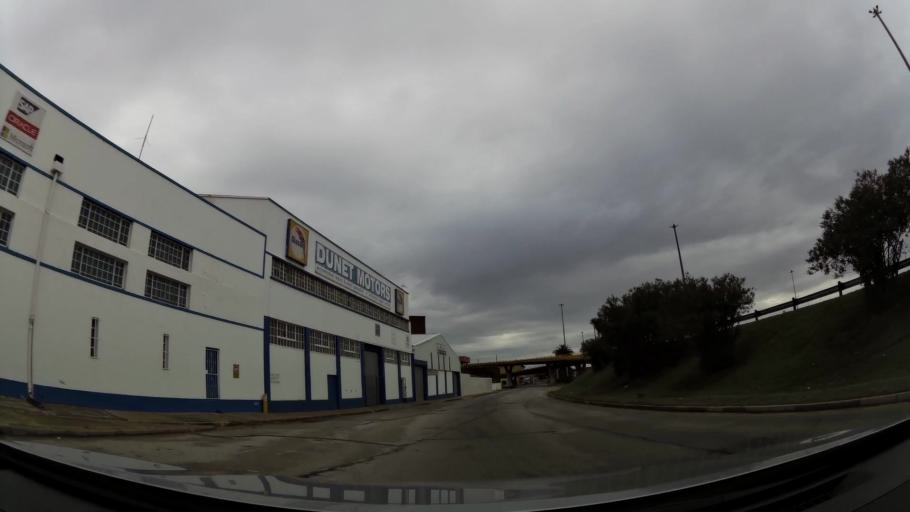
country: ZA
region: Eastern Cape
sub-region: Nelson Mandela Bay Metropolitan Municipality
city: Port Elizabeth
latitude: -33.9540
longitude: 25.6143
